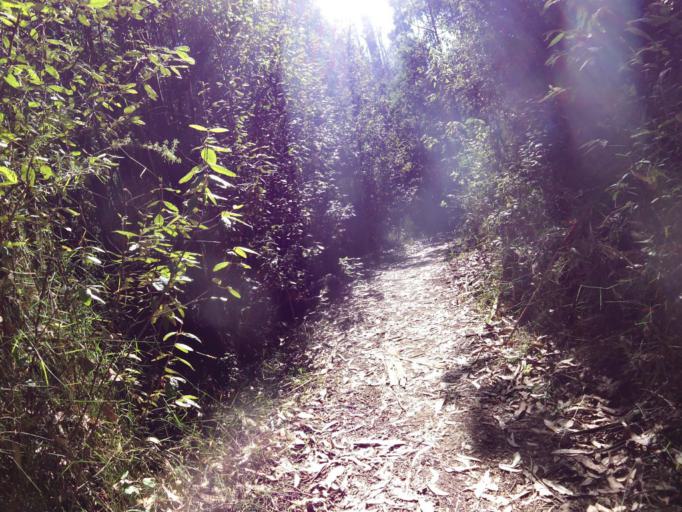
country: AU
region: Victoria
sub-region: Yarra Ranges
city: Millgrove
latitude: -37.5018
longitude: 145.8328
